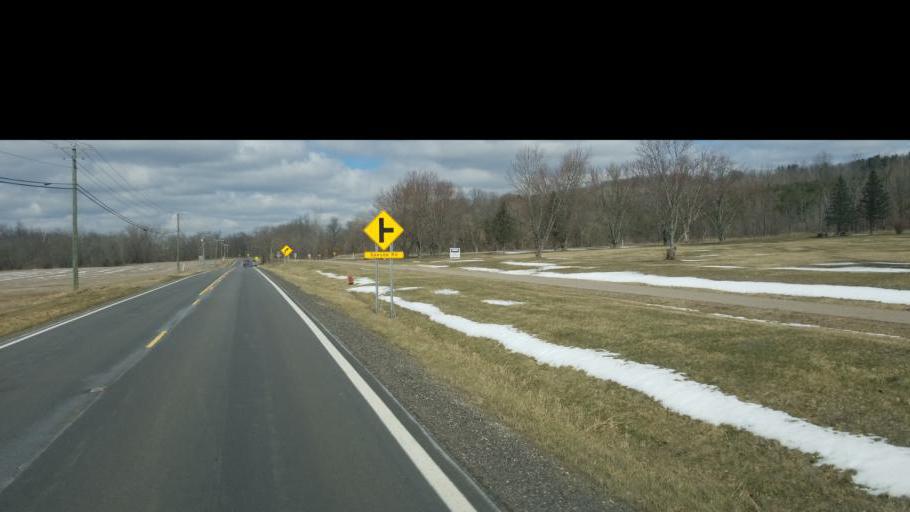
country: US
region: Ohio
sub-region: Sandusky County
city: Bellville
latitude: 40.6348
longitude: -82.5388
